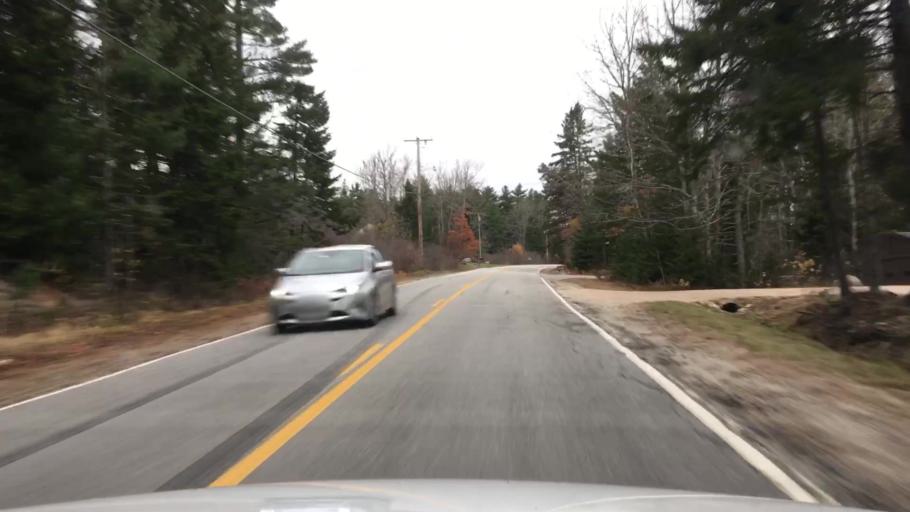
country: US
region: Maine
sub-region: Hancock County
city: Sedgwick
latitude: 44.2872
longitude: -68.5552
